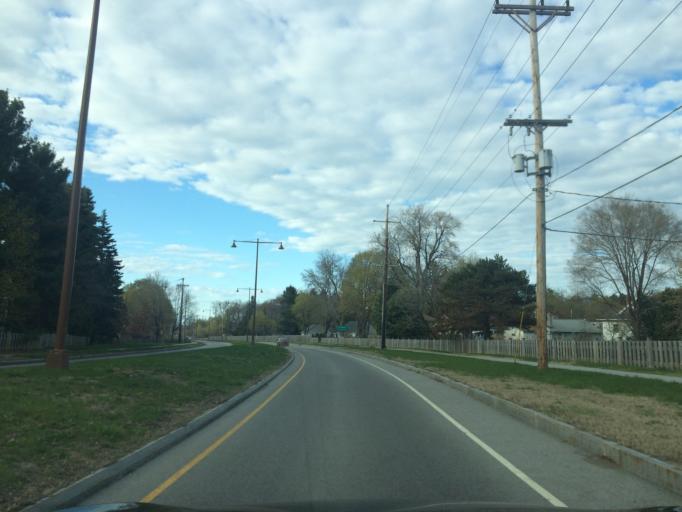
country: US
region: New York
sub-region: Monroe County
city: Irondequoit
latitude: 43.2175
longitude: -77.5457
